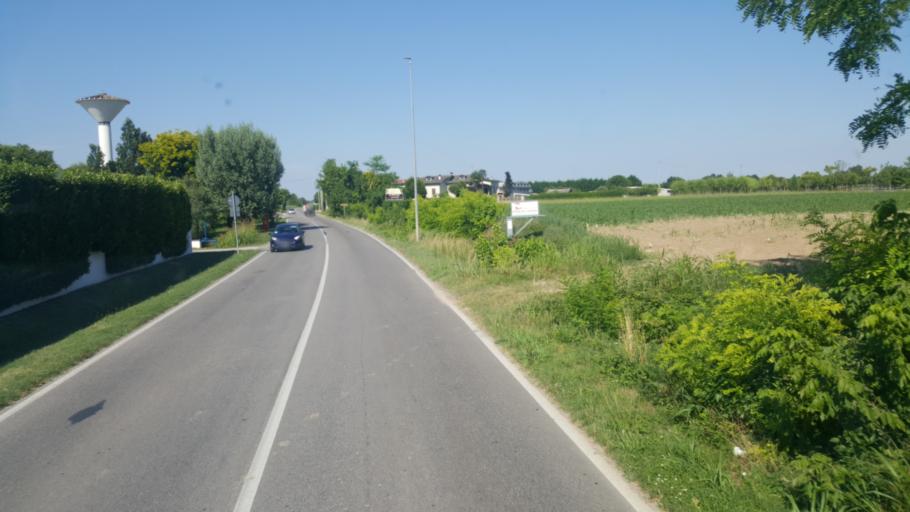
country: IT
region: Lombardy
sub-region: Provincia di Mantova
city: Casalromano
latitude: 45.2001
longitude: 10.3712
